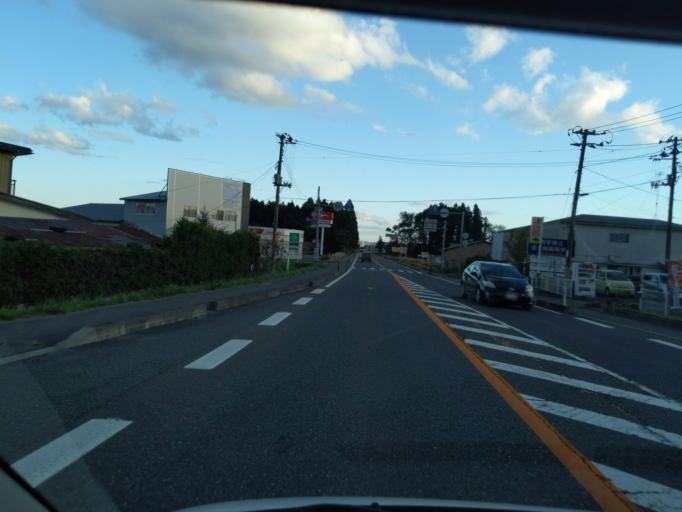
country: JP
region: Iwate
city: Kitakami
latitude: 39.2148
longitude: 141.1028
